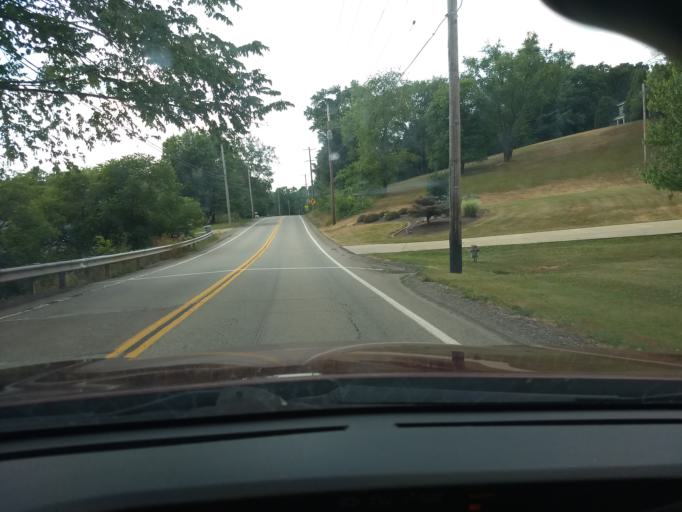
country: US
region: Pennsylvania
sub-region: Allegheny County
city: Curtisville
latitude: 40.6292
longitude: -79.8644
